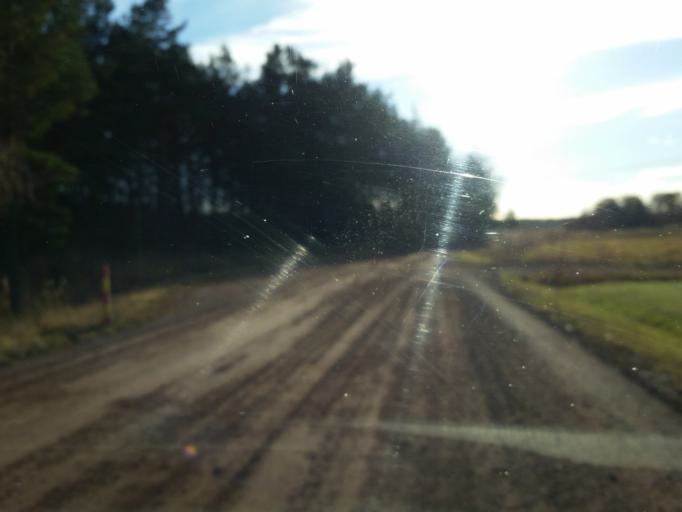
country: AX
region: Alands skaergard
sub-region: Kumlinge
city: Kumlinge
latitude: 60.2507
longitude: 20.7958
